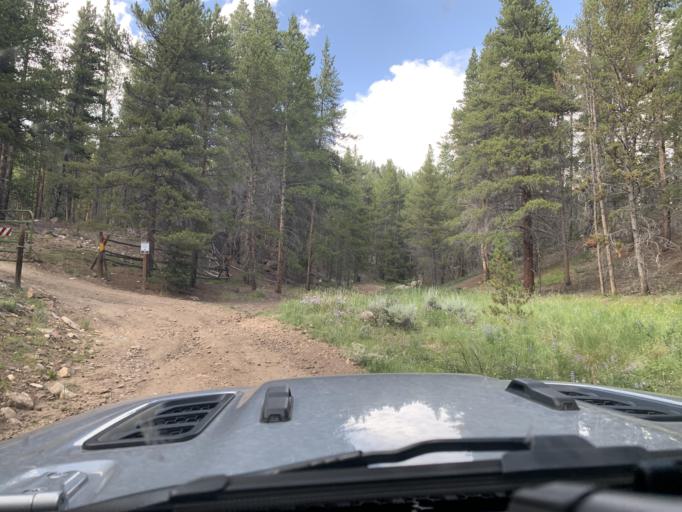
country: US
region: Colorado
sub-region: Lake County
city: Leadville North
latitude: 39.2757
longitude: -106.3098
